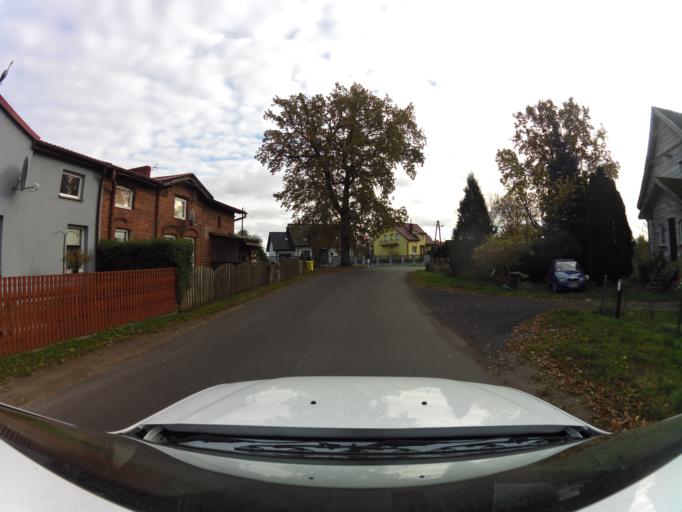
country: PL
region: West Pomeranian Voivodeship
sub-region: Powiat gryficki
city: Gryfice
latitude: 53.9782
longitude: 15.2116
